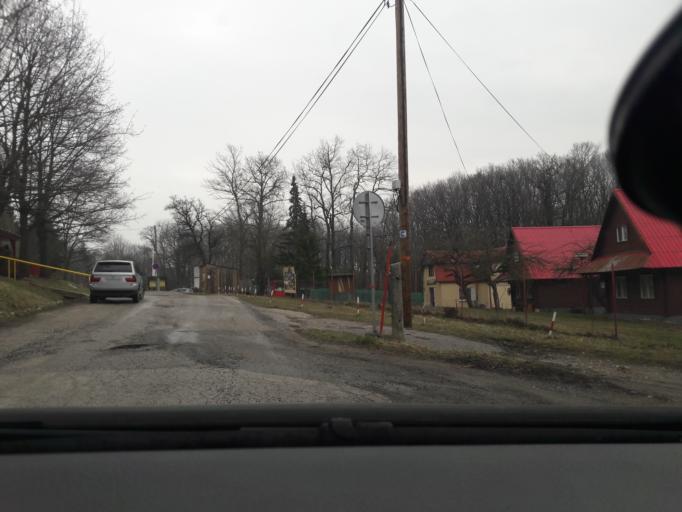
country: SK
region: Trnavsky
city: Smolenice
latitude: 48.4942
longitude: 17.4011
